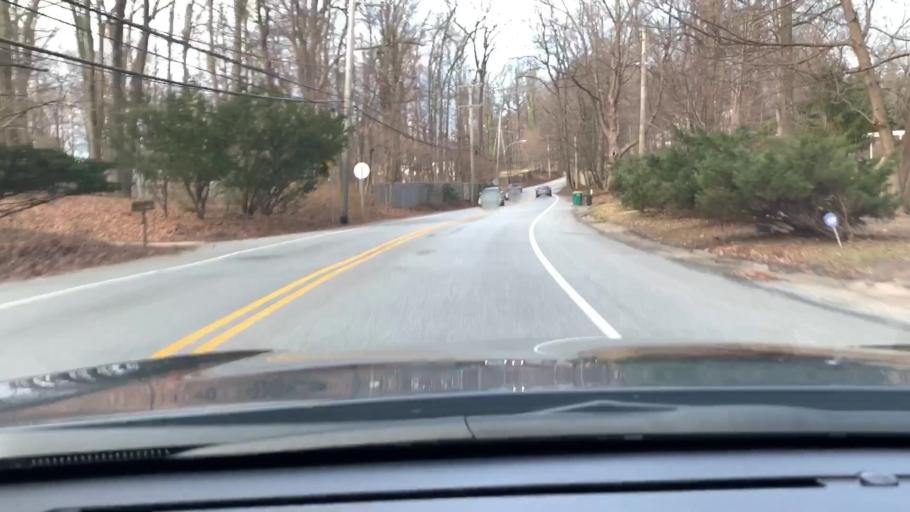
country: US
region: Pennsylvania
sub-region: Chester County
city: Paoli
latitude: 40.0359
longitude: -75.4764
